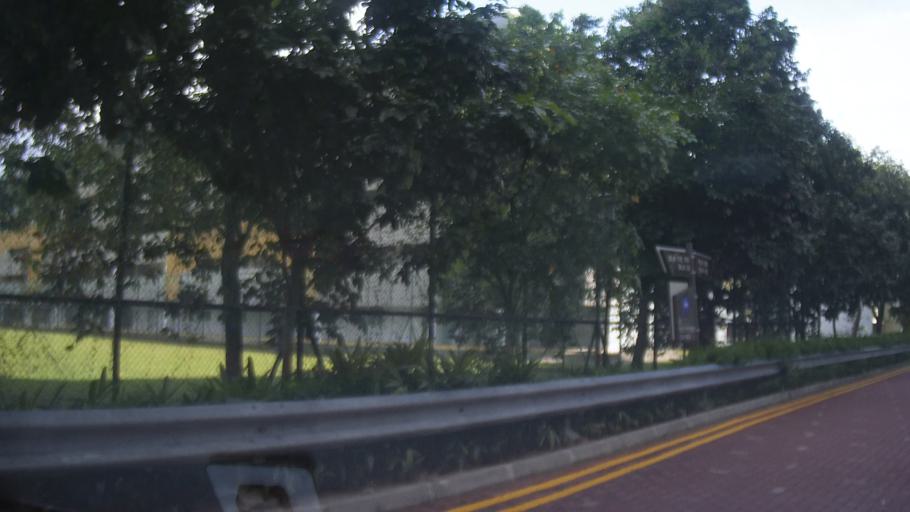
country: SG
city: Singapore
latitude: 1.3293
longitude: 103.8893
